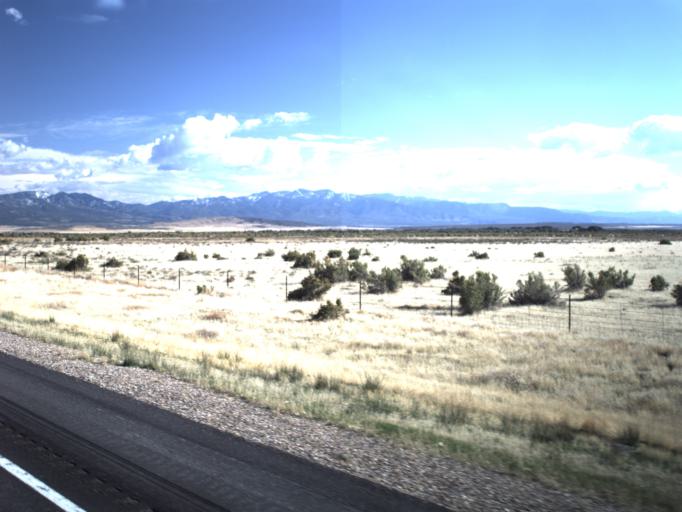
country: US
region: Utah
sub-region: Millard County
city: Fillmore
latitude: 39.1528
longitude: -112.4024
